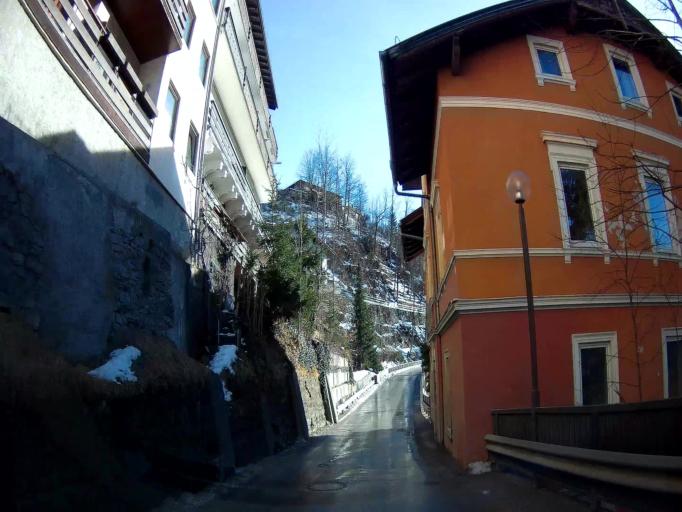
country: AT
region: Salzburg
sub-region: Politischer Bezirk Sankt Johann im Pongau
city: Bad Gastein
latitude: 47.1178
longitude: 13.1377
